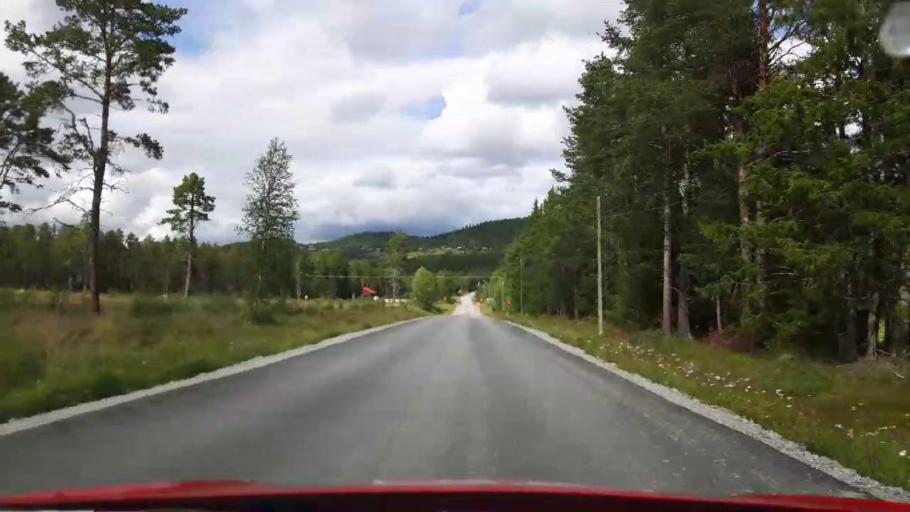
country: NO
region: Hedmark
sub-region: Engerdal
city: Engerdal
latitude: 62.4316
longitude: 12.6798
